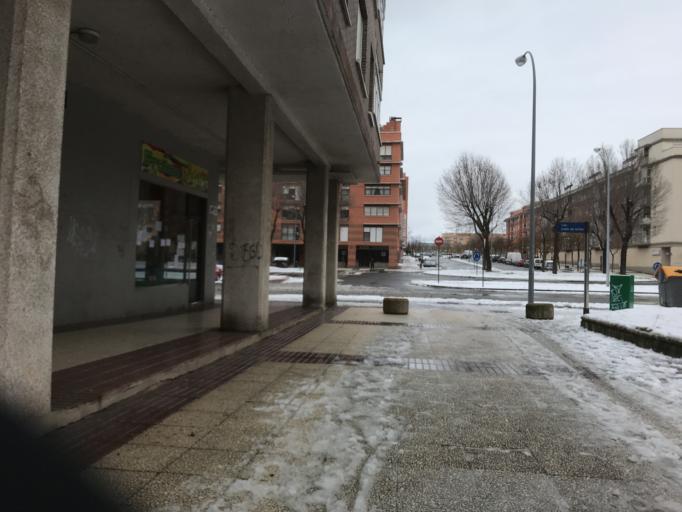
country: ES
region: Basque Country
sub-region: Provincia de Alava
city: Gasteiz / Vitoria
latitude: 42.8591
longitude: -2.6955
